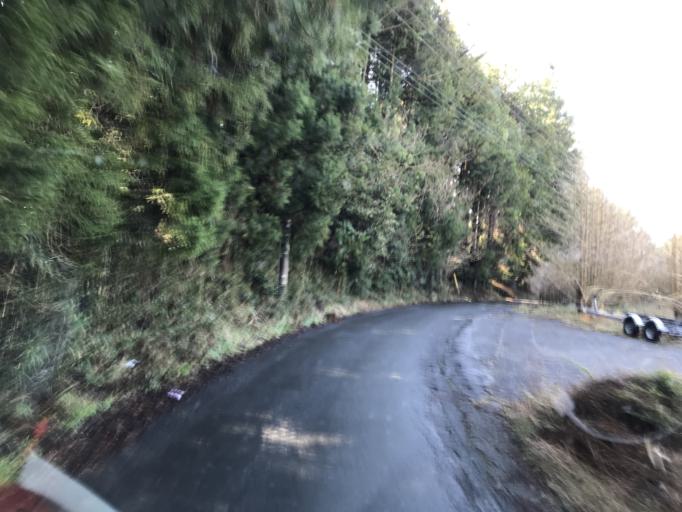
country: JP
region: Shizuoka
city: Fujinomiya
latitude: 35.2460
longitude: 138.6614
